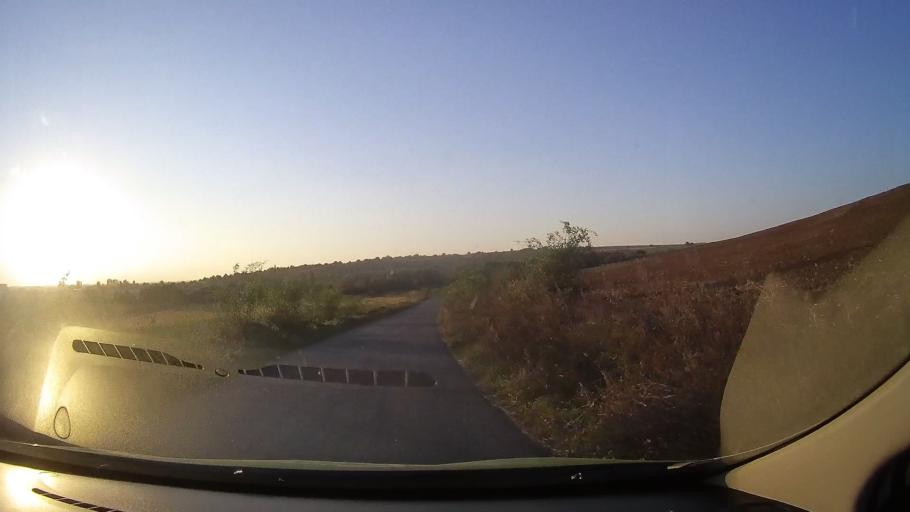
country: RO
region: Bihor
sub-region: Comuna Salard
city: Salard
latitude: 47.2491
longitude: 22.0158
